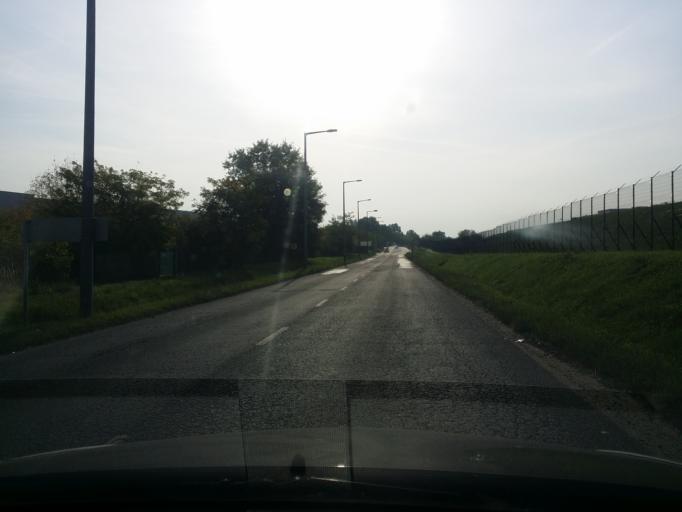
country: HU
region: Budapest
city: Budapest XV. keruelet
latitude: 47.5828
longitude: 19.1360
